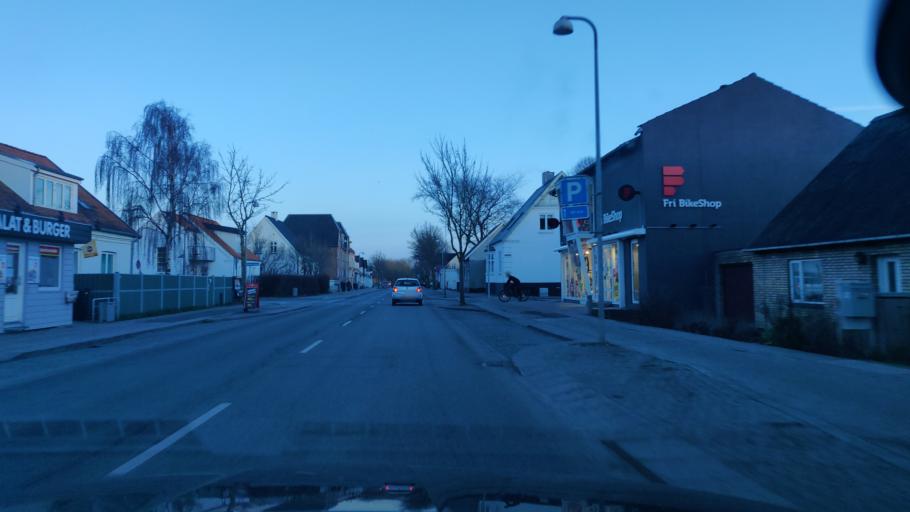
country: DK
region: North Denmark
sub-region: Alborg Kommune
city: Aalborg
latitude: 57.0652
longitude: 9.9055
